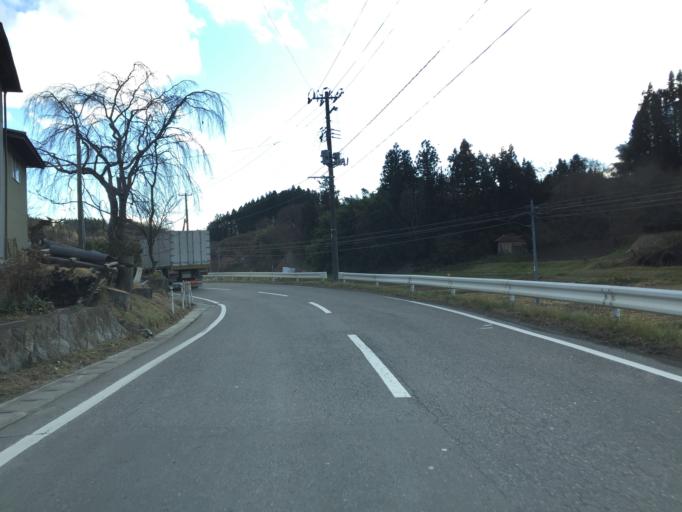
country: JP
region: Fukushima
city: Funehikimachi-funehiki
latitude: 37.5067
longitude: 140.5780
